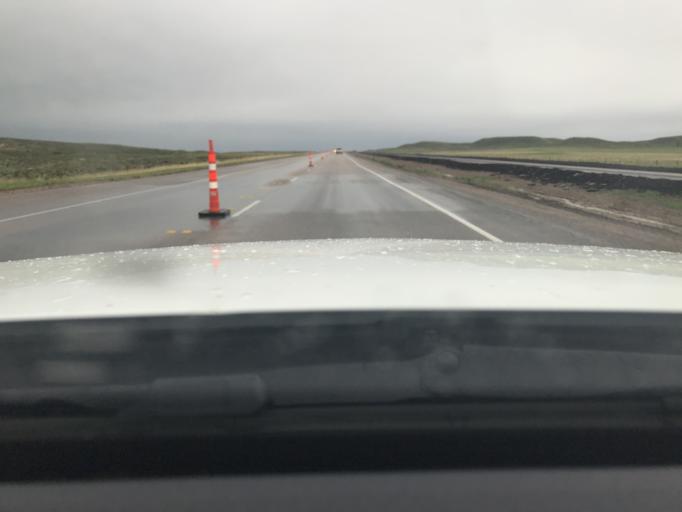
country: US
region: Wyoming
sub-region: Converse County
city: Douglas
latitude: 42.7934
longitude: -105.5759
